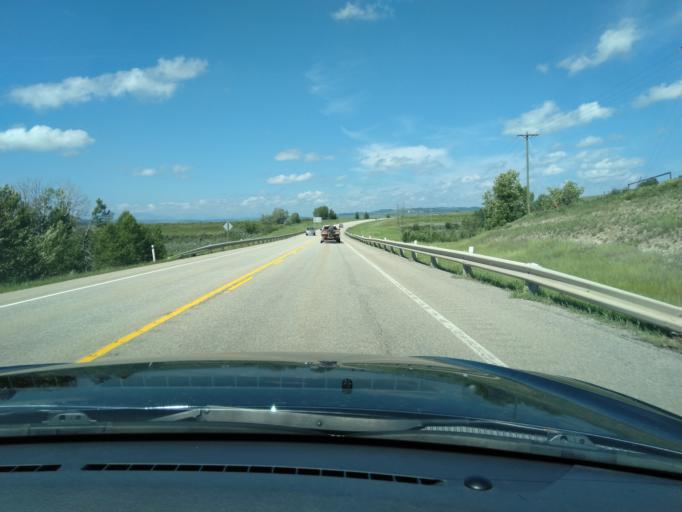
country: CA
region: Alberta
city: Cochrane
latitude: 51.2079
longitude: -114.5179
